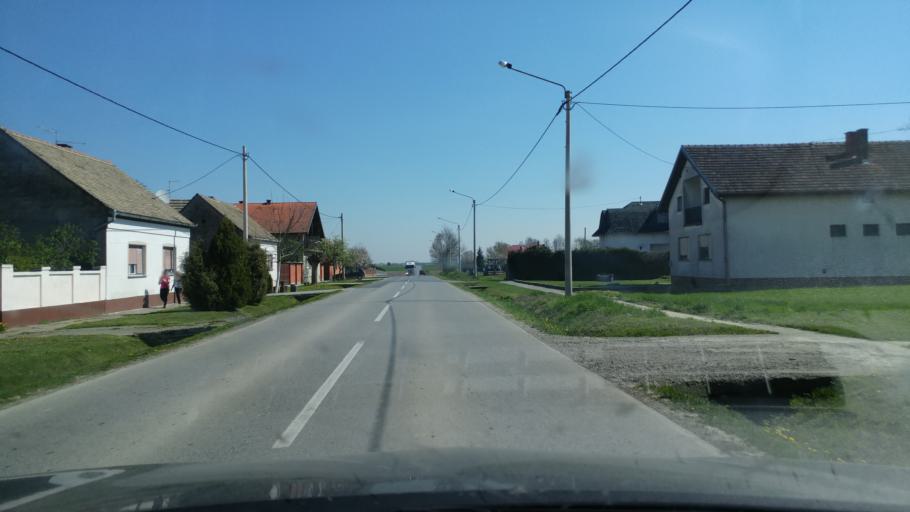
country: HR
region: Osjecko-Baranjska
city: Viskovci
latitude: 45.3503
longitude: 18.4998
